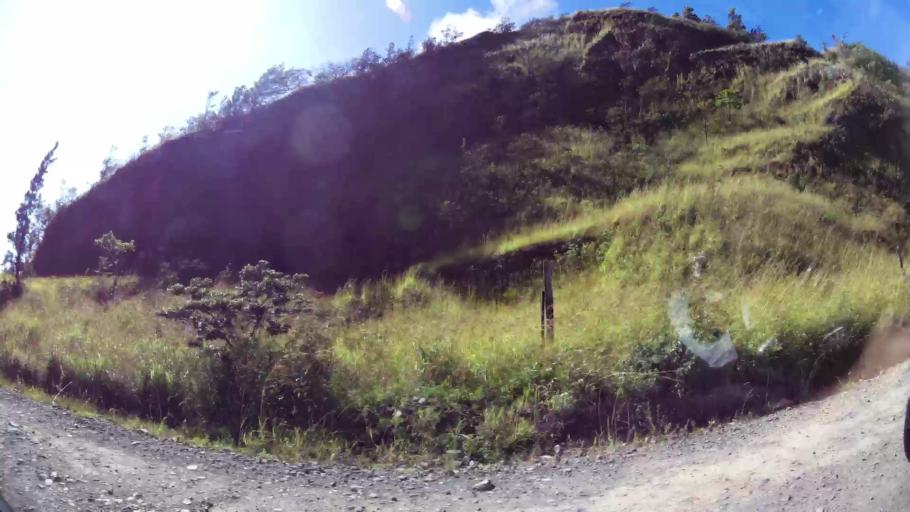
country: CR
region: Guanacaste
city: Juntas
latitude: 10.3334
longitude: -84.8528
